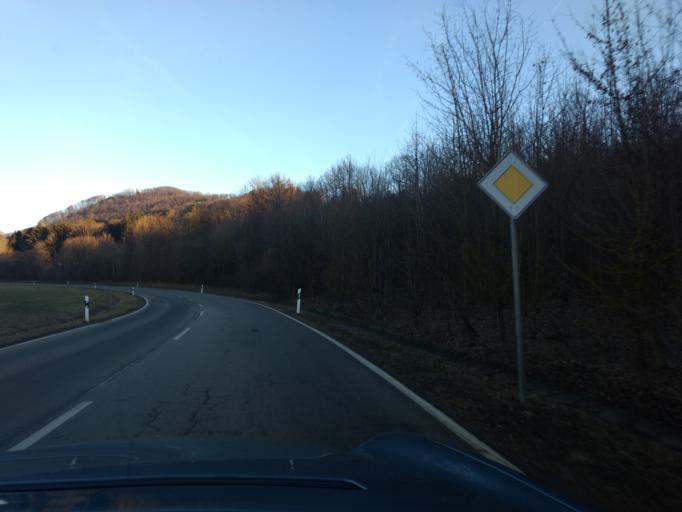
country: DE
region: Baden-Wuerttemberg
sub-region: Regierungsbezirk Stuttgart
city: Ottenbach
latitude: 48.7610
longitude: 9.7666
